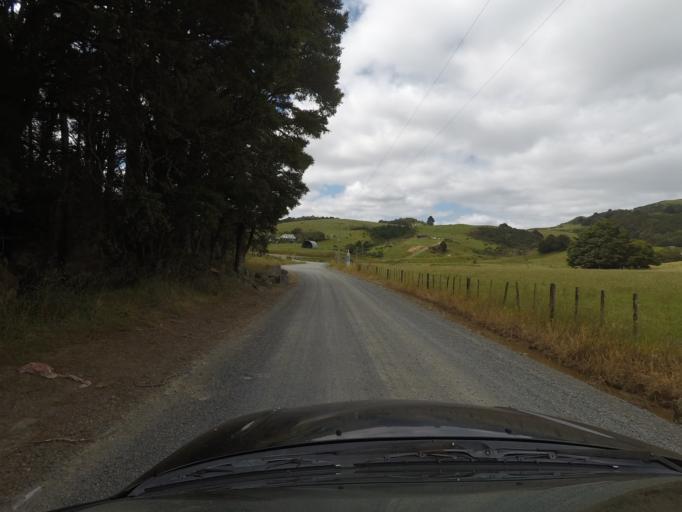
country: NZ
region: Northland
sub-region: Whangarei
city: Ruakaka
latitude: -35.9341
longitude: 174.3477
